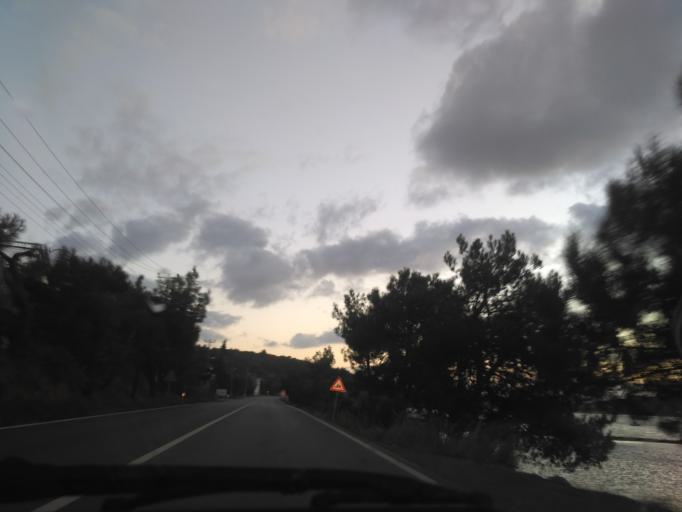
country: TR
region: Balikesir
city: Ayvalik
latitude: 39.2837
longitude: 26.6739
